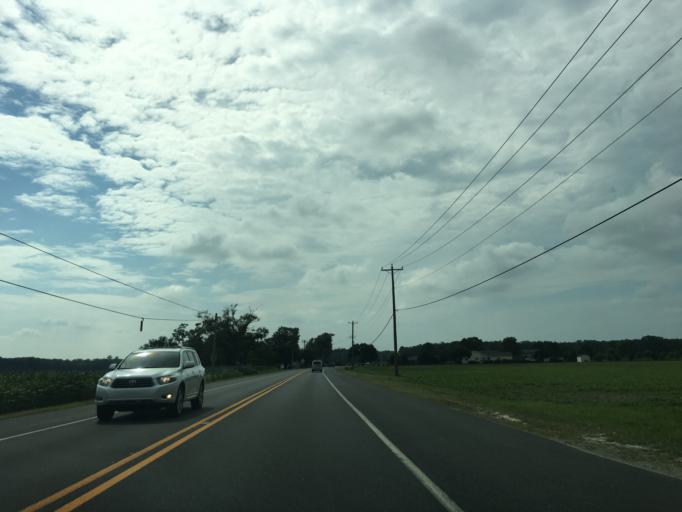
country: US
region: Delaware
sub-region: Sussex County
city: Millsboro
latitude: 38.5552
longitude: -75.2532
